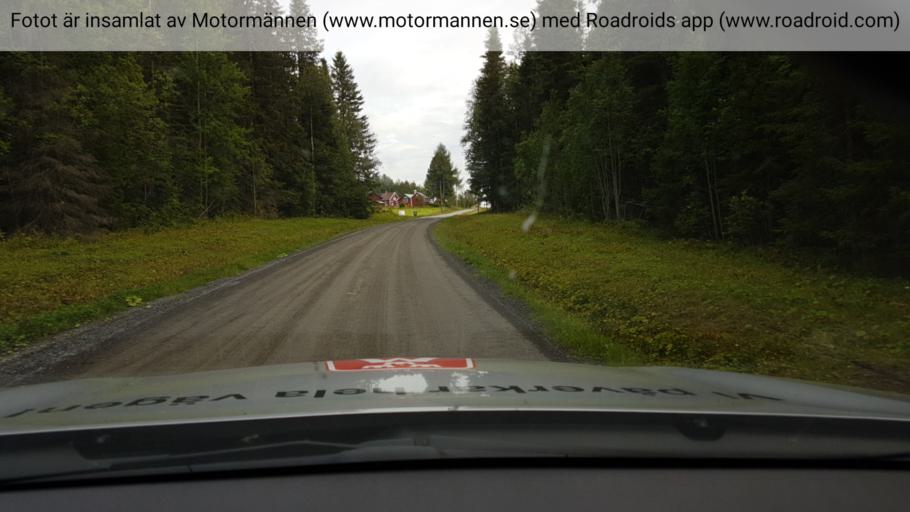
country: SE
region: Jaemtland
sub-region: OEstersunds Kommun
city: Lit
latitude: 63.6461
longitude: 14.9518
